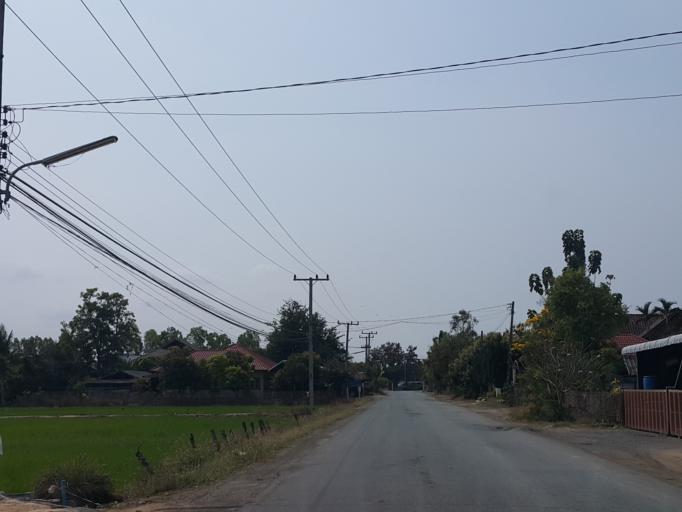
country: TH
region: Lamphun
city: Ban Thi
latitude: 18.6790
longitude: 99.1010
